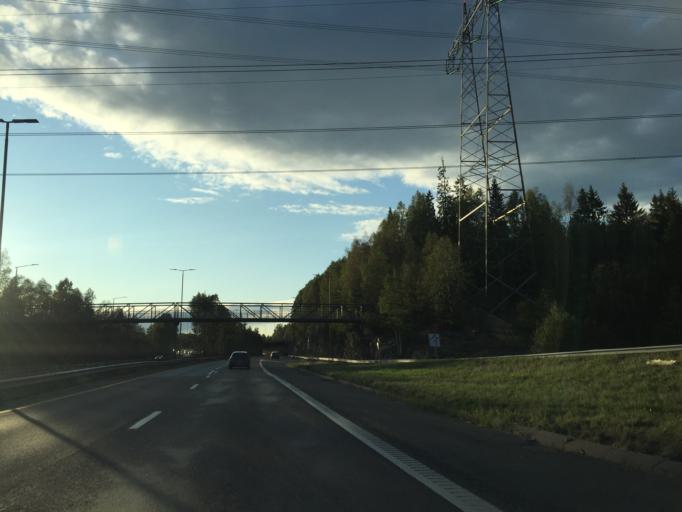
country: NO
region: Akershus
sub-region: Lorenskog
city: Kjenn
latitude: 59.9373
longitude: 10.9343
